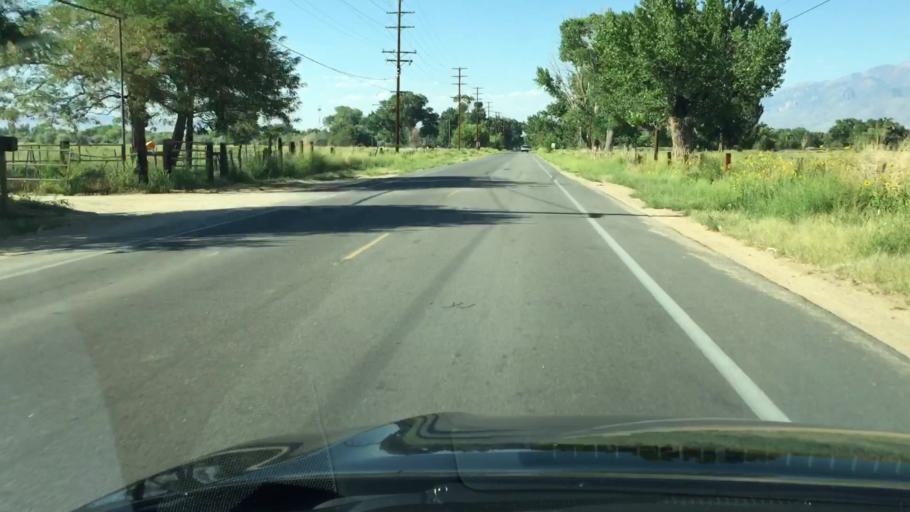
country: US
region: California
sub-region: Inyo County
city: Bishop
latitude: 37.3507
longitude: -118.4046
